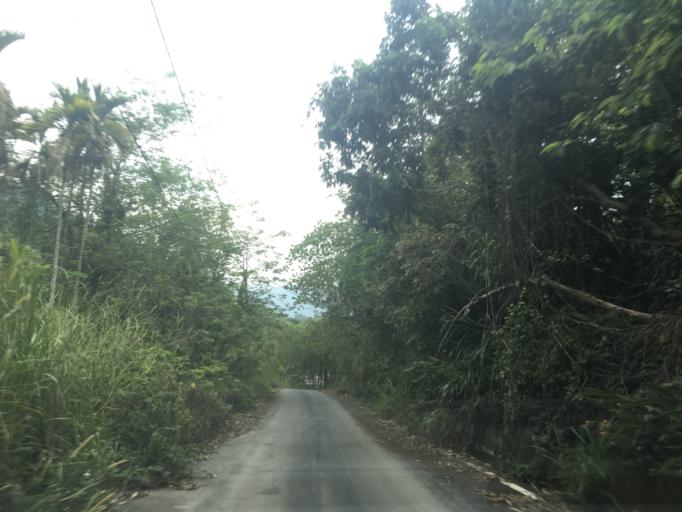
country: TW
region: Taiwan
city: Zhongxing New Village
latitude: 24.0442
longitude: 120.8081
